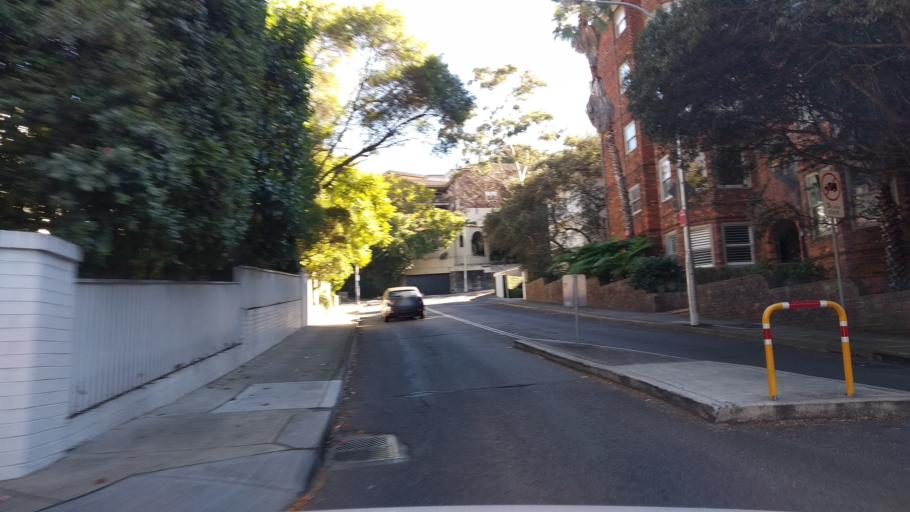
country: AU
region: New South Wales
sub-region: Woollahra
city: Darling Point
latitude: -33.8772
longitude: 151.2386
